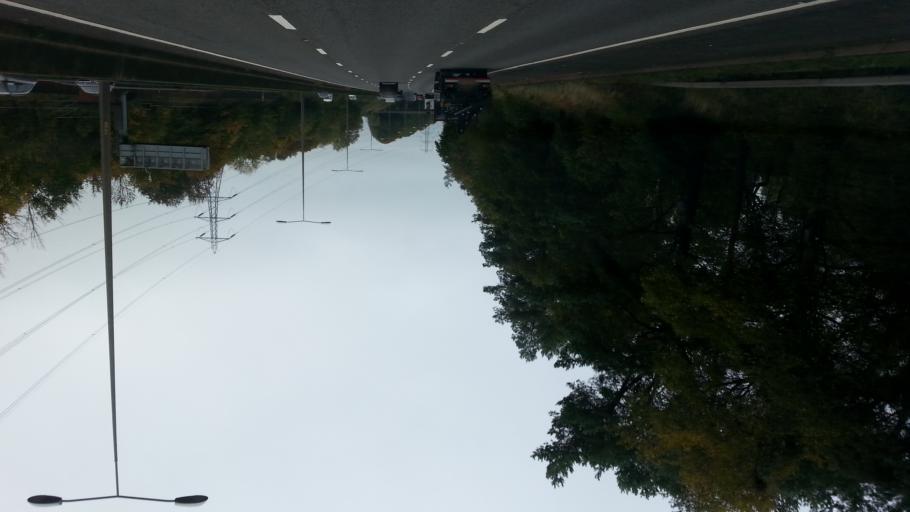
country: GB
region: England
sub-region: City and Borough of Birmingham
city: Bartley Green
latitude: 52.4098
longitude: -2.0293
